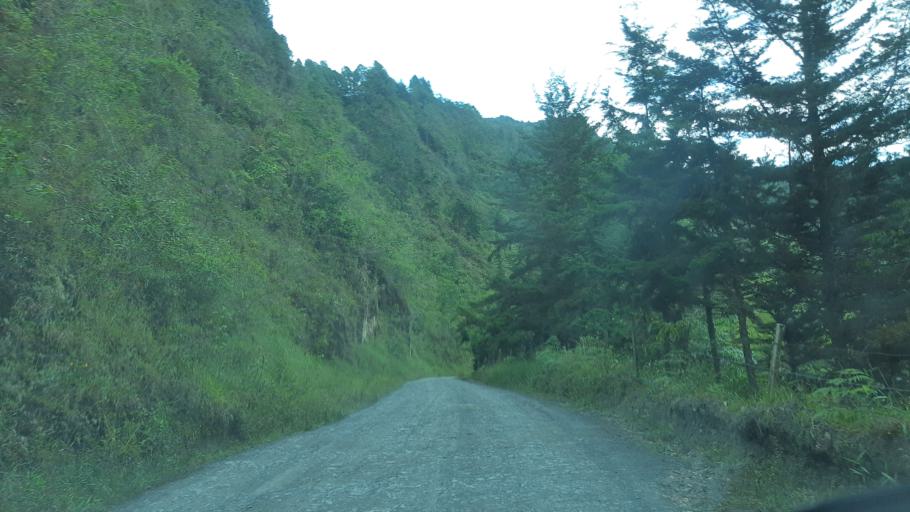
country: CO
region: Boyaca
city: Garagoa
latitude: 4.9871
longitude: -73.3290
